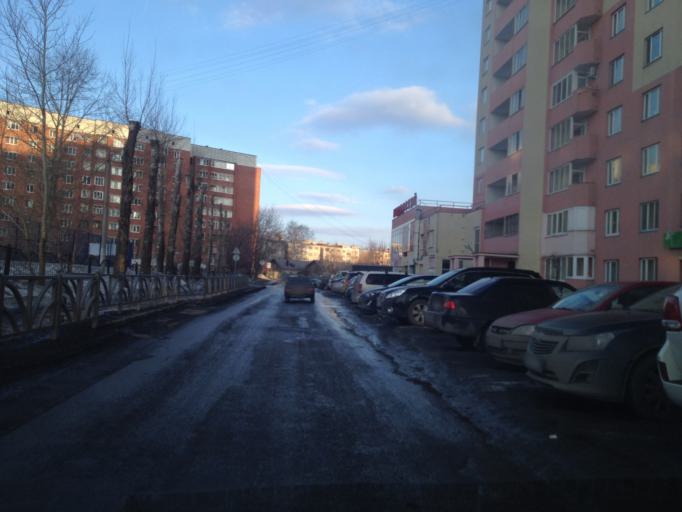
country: RU
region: Sverdlovsk
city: Sovkhoznyy
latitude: 56.7644
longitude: 60.5982
